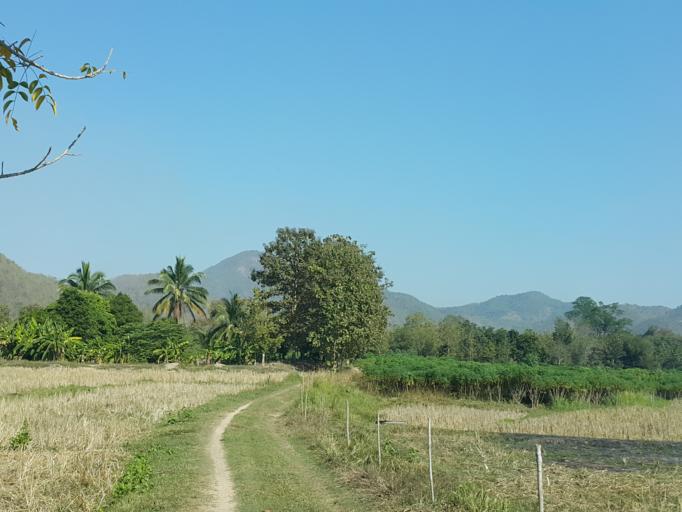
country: TH
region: Sukhothai
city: Thung Saliam
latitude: 17.3257
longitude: 99.4608
